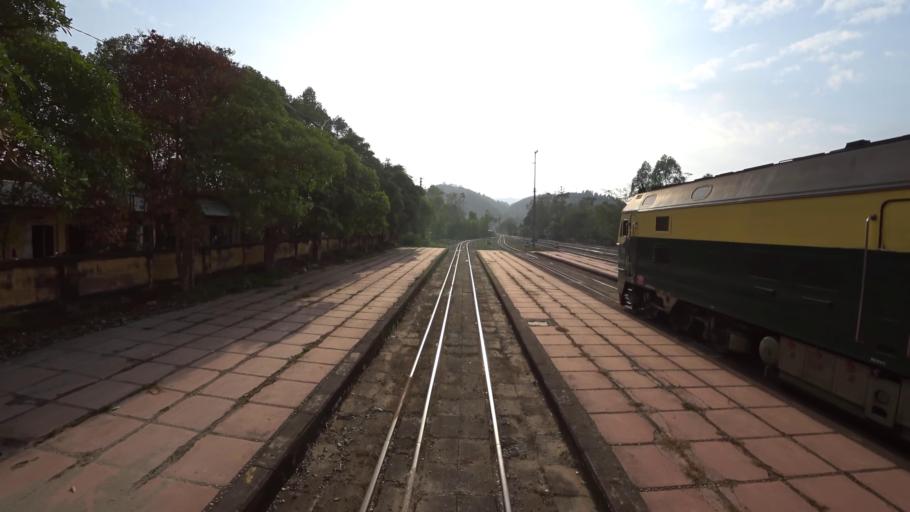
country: VN
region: Lang Son
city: Thi Tran Cao Loc
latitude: 21.9423
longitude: 106.6958
